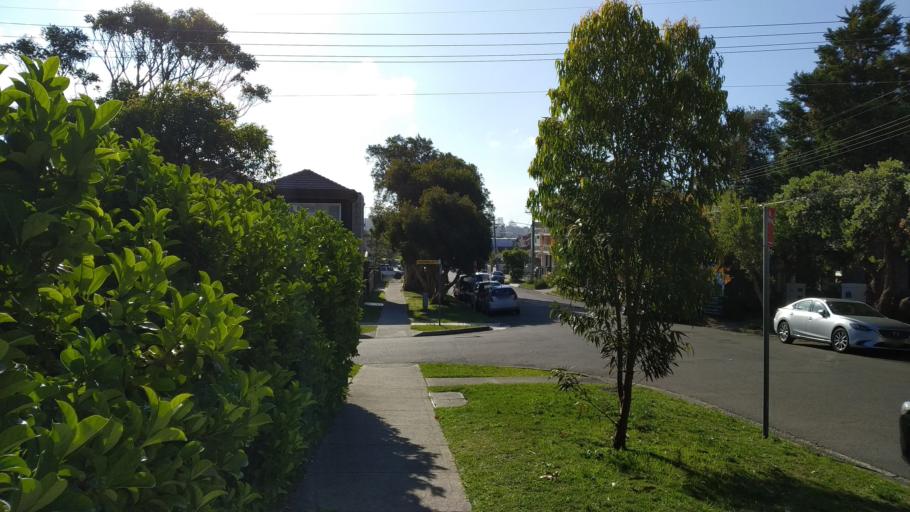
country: AU
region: New South Wales
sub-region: Waverley
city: North Bondi
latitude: -33.8827
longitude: 151.2803
